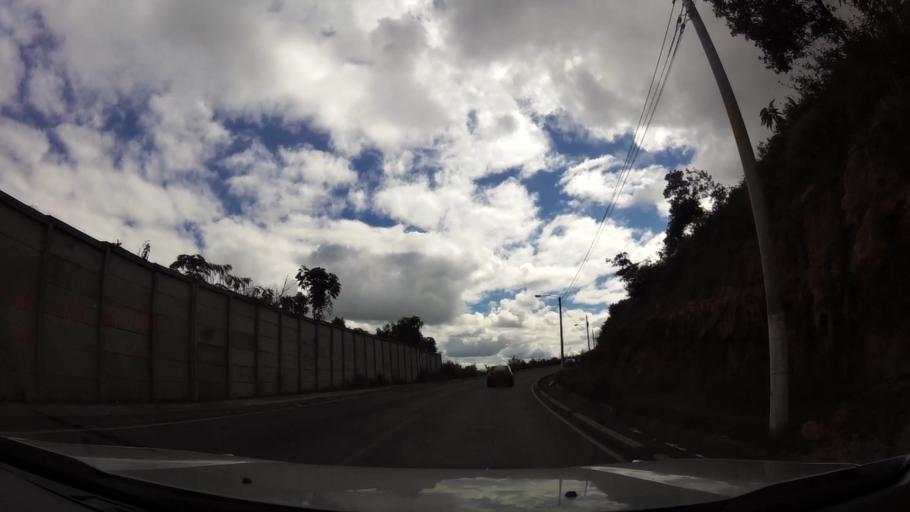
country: GT
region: Guatemala
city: Guatemala City
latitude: 14.6647
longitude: -90.5514
